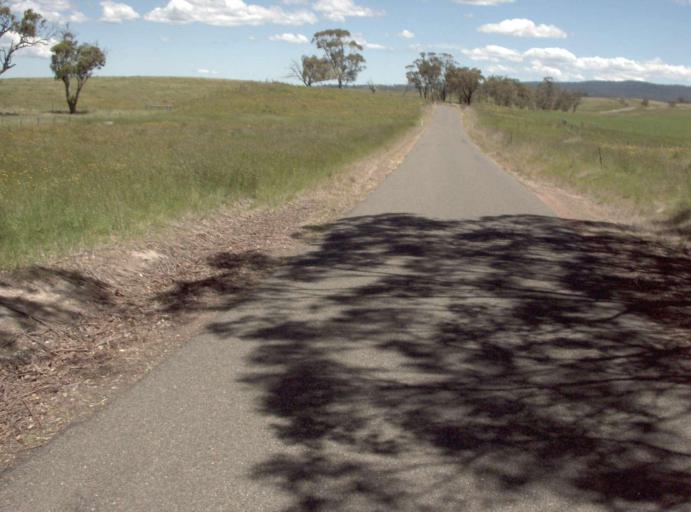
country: AU
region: New South Wales
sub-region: Snowy River
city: Jindabyne
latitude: -37.0826
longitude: 148.2751
